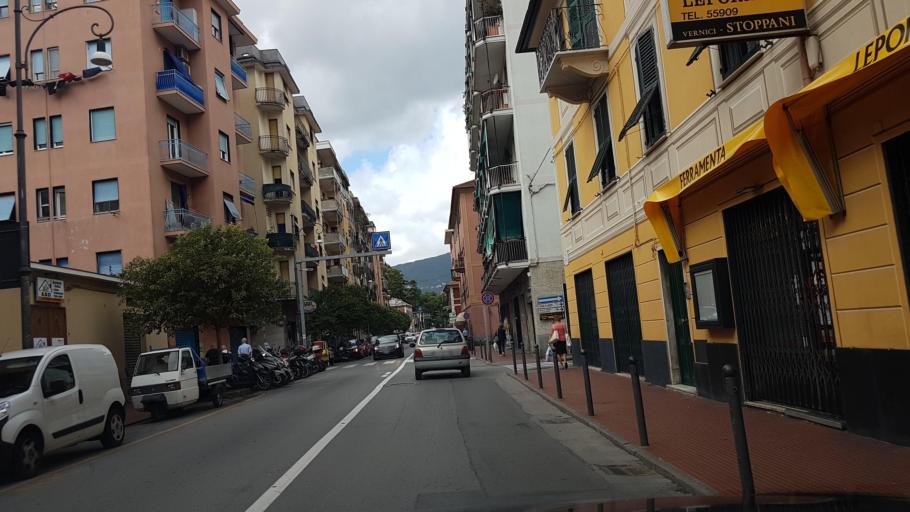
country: IT
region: Liguria
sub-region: Provincia di Genova
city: Rapallo
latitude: 44.3522
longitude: 9.2206
